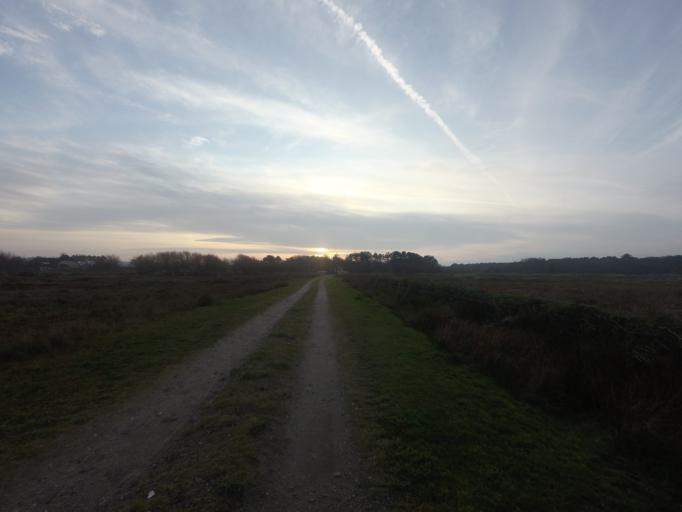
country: NL
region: North Holland
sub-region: Gemeente Texel
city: Den Burg
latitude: 53.1054
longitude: 4.7743
